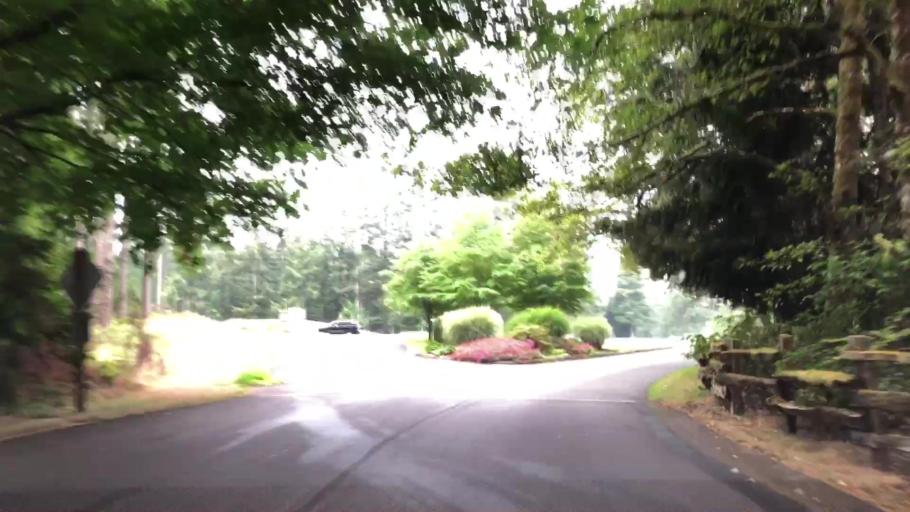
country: US
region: Washington
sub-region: Kitsap County
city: Navy Yard City
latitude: 47.5210
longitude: -122.7463
